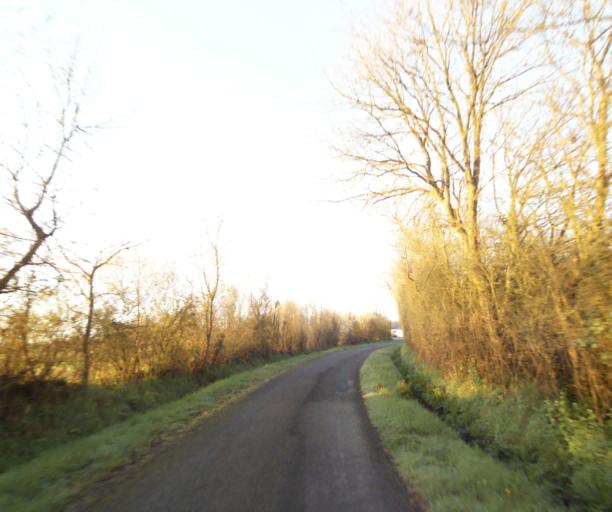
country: FR
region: Pays de la Loire
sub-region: Departement de la Loire-Atlantique
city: Bouvron
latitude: 47.4256
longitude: -1.8827
